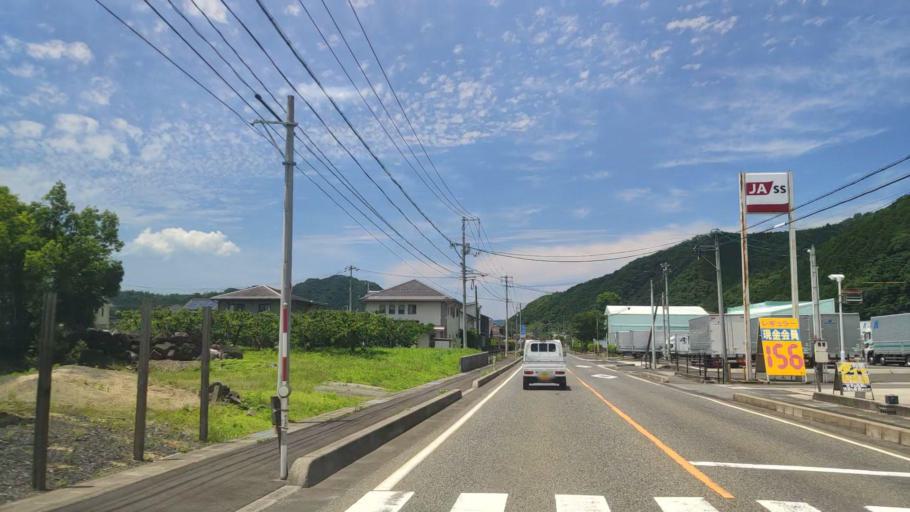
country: JP
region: Tottori
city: Tottori
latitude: 35.3739
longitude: 134.3051
